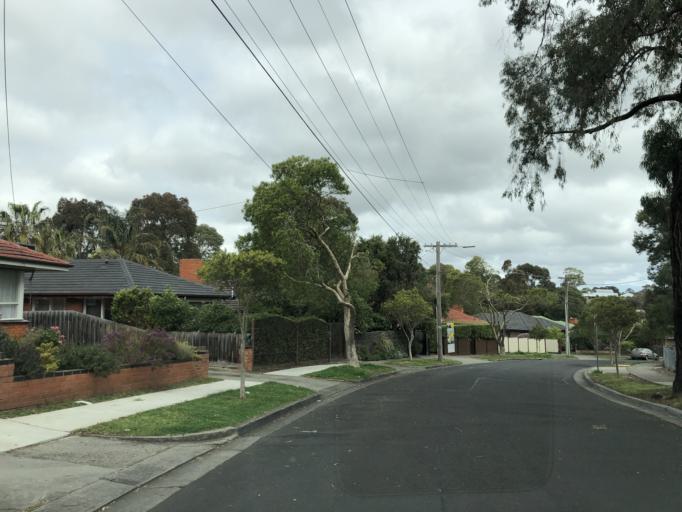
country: AU
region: Victoria
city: Burwood East
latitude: -37.8481
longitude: 145.1486
